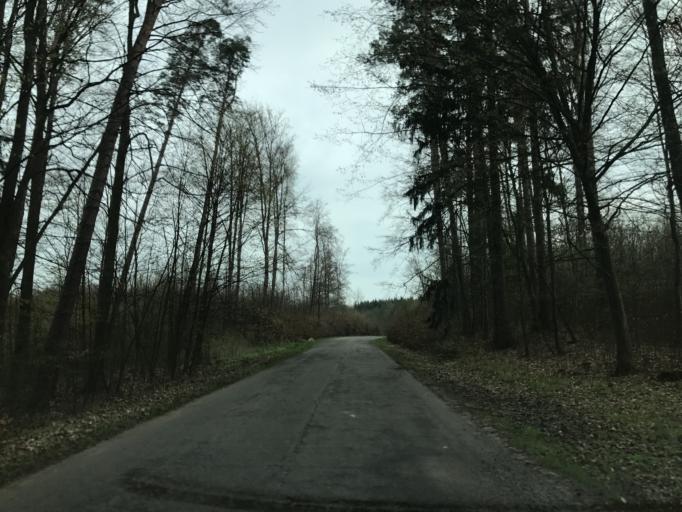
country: PL
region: Warmian-Masurian Voivodeship
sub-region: Powiat ostrodzki
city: Gierzwald
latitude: 53.6396
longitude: 20.0898
